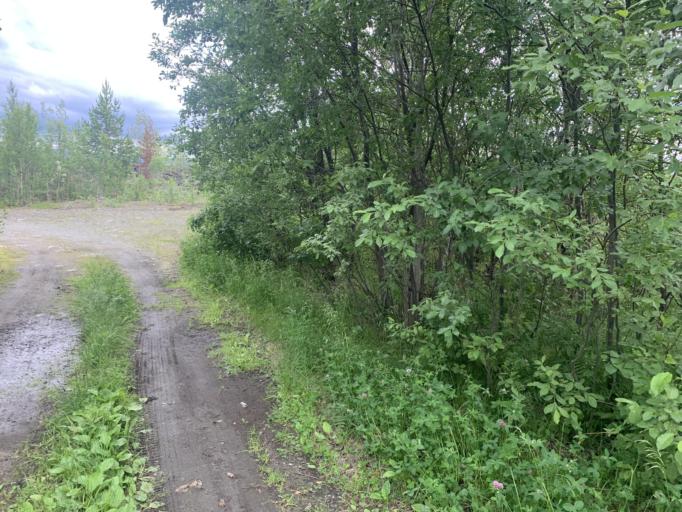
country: RU
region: Murmansk
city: Monchegorsk
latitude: 67.8738
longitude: 33.0859
